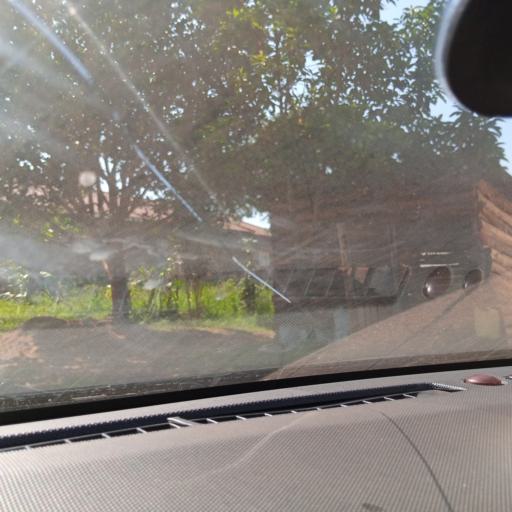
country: UG
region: Central Region
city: Masaka
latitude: -0.3294
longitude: 31.7315
